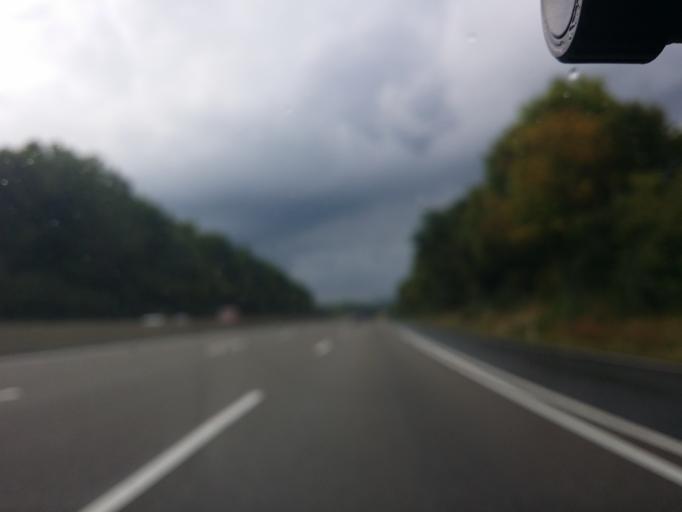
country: DE
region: Hesse
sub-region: Regierungsbezirk Kassel
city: Kirchheim
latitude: 50.9120
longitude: 9.5733
